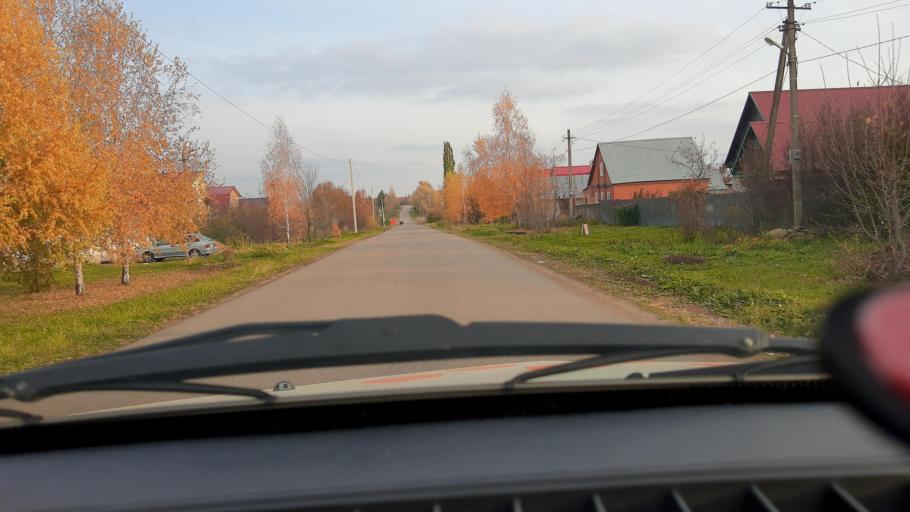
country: RU
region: Bashkortostan
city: Iglino
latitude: 54.7965
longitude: 56.3134
